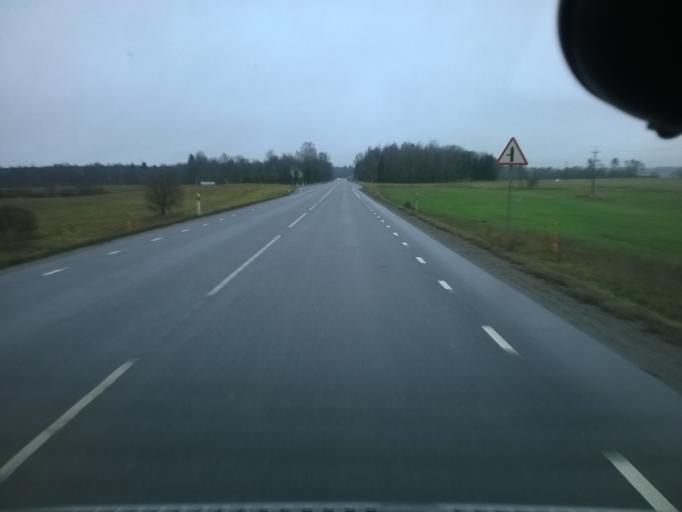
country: EE
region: Harju
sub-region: Saku vald
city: Saku
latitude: 59.2875
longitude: 24.7402
